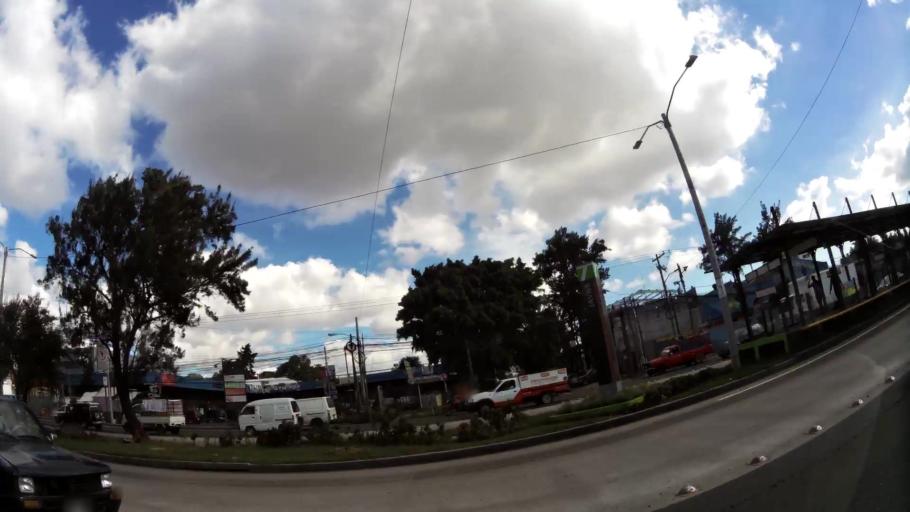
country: GT
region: Guatemala
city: Mixco
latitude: 14.5875
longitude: -90.5626
